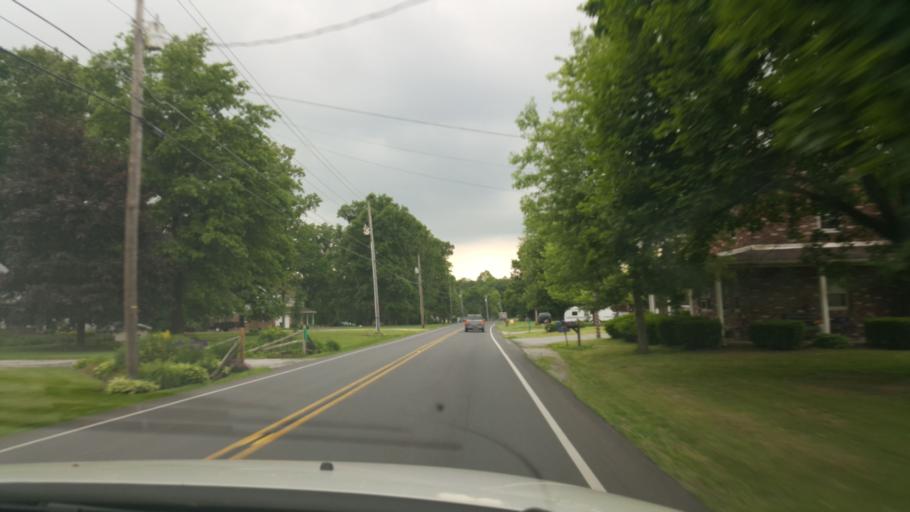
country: US
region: Pennsylvania
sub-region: Adams County
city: Lake Meade
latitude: 39.9497
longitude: -77.1084
